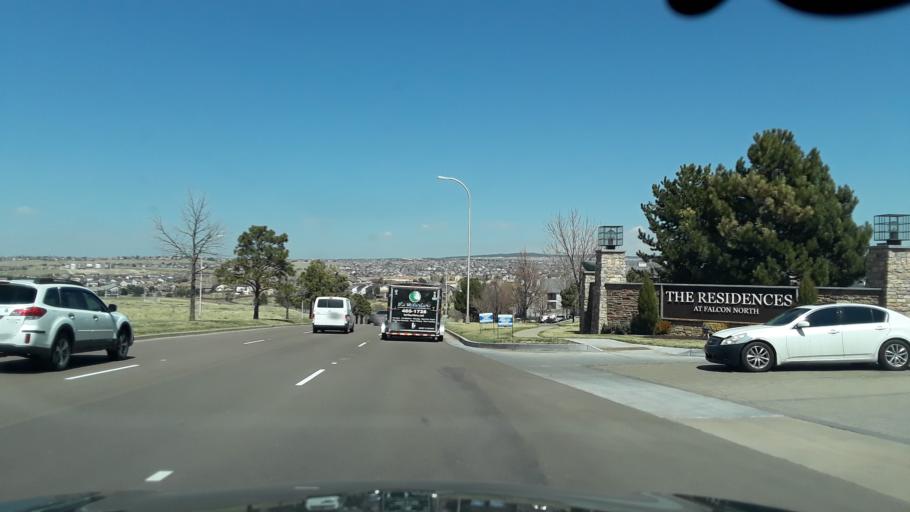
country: US
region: Colorado
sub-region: El Paso County
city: Cimarron Hills
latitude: 38.9227
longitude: -104.7384
